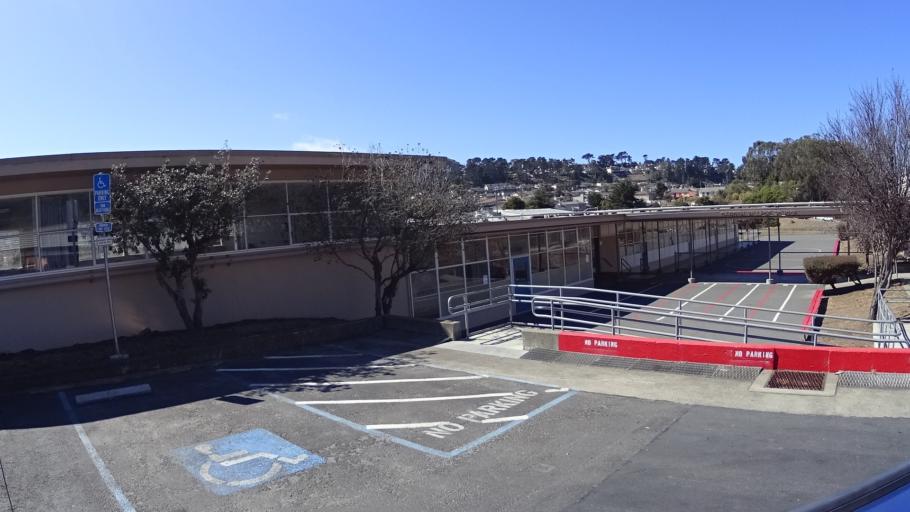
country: US
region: California
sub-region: San Mateo County
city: Broadmoor
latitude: 37.6943
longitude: -122.4776
